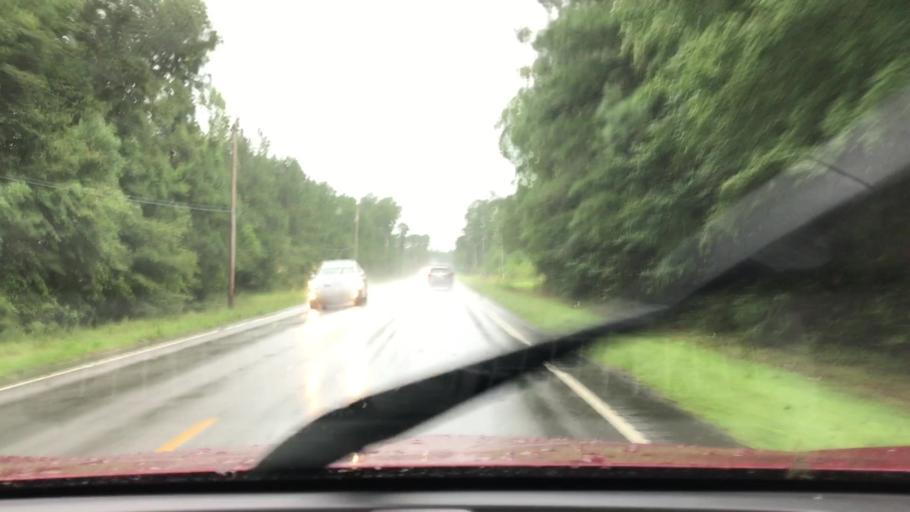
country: US
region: South Carolina
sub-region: Horry County
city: Conway
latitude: 33.7880
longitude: -79.0758
